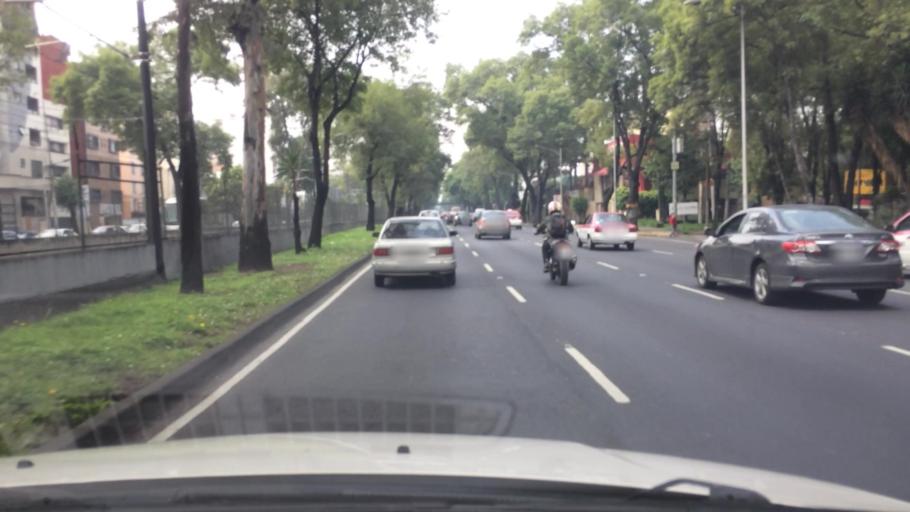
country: MX
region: Mexico City
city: Coyoacan
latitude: 19.3354
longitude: -99.1419
